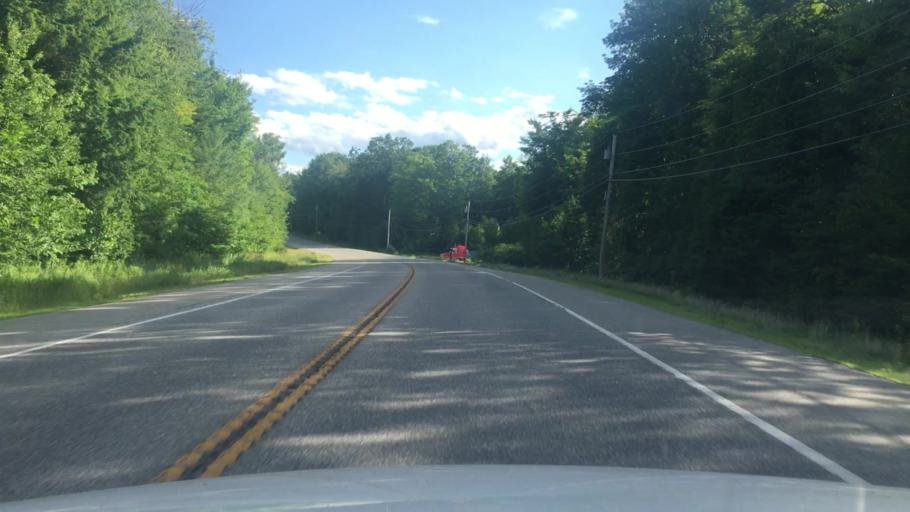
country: US
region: Maine
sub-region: Androscoggin County
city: Livermore
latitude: 44.4238
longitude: -70.2195
